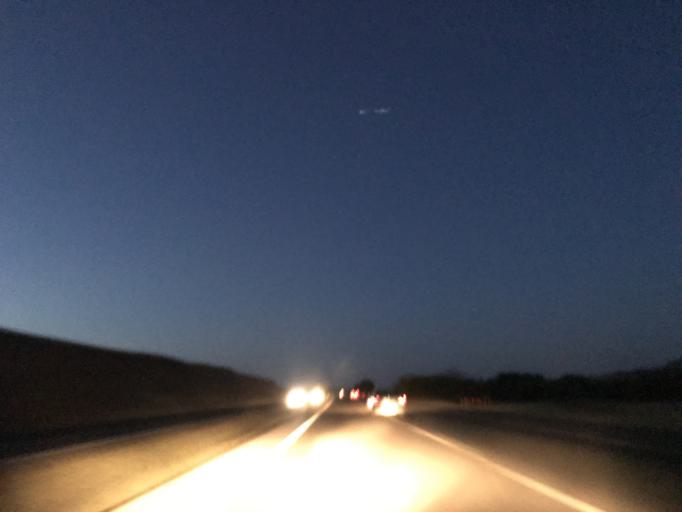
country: TR
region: Yozgat
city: Yerkoy
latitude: 39.6671
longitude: 34.5707
